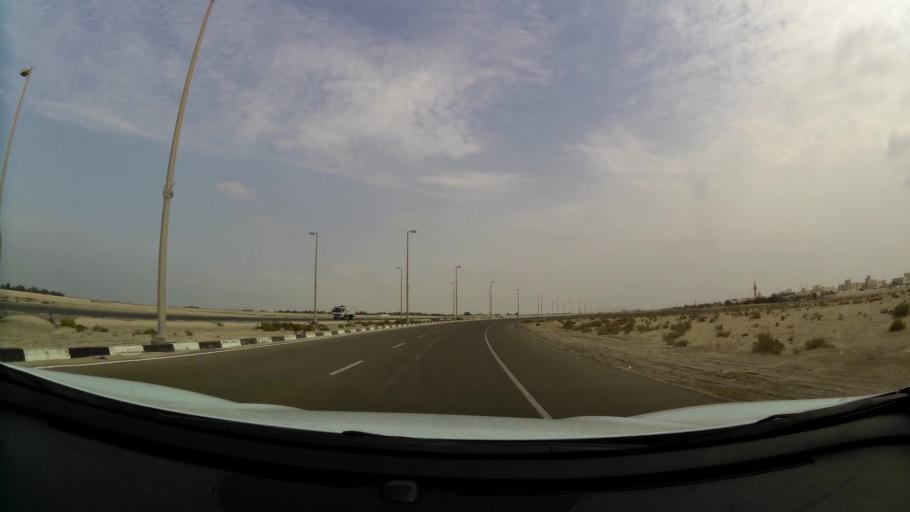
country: AE
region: Abu Dhabi
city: Abu Dhabi
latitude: 24.6421
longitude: 54.6650
